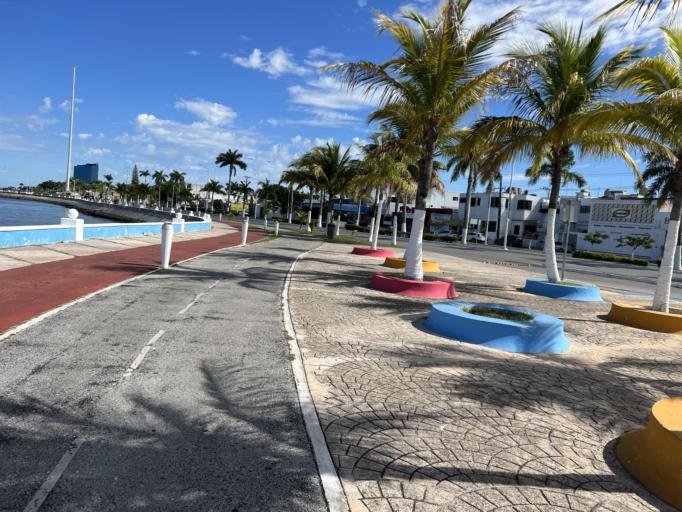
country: MX
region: Campeche
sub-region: Campeche
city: Campeche
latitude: 19.8402
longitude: -90.5481
